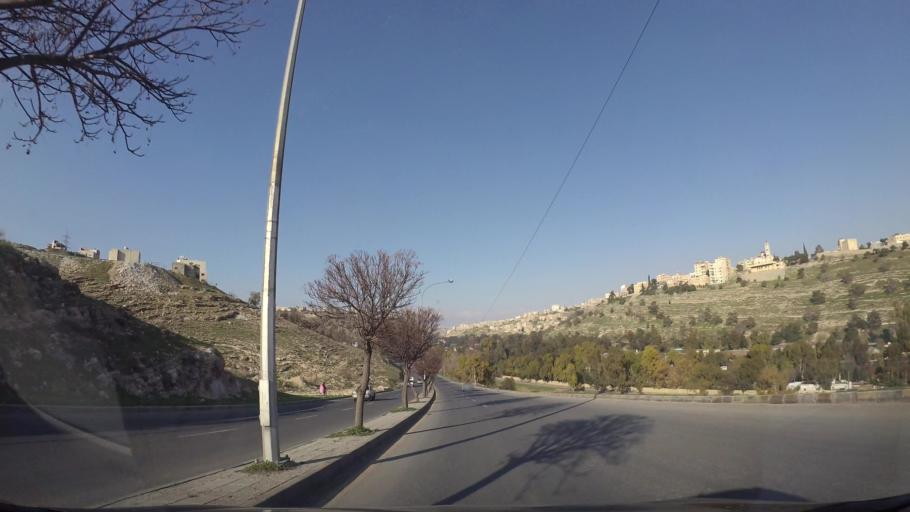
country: JO
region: Amman
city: Amman
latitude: 31.9753
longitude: 35.9696
